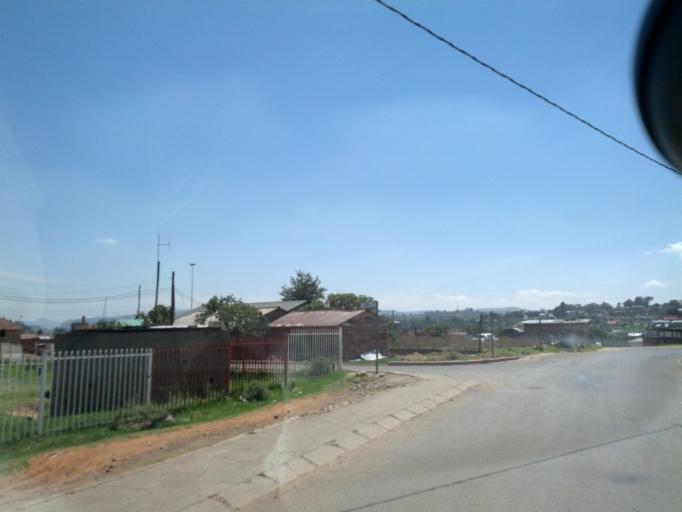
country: LS
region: Butha-Buthe
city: Butha-Buthe
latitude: -28.7619
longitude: 28.2477
